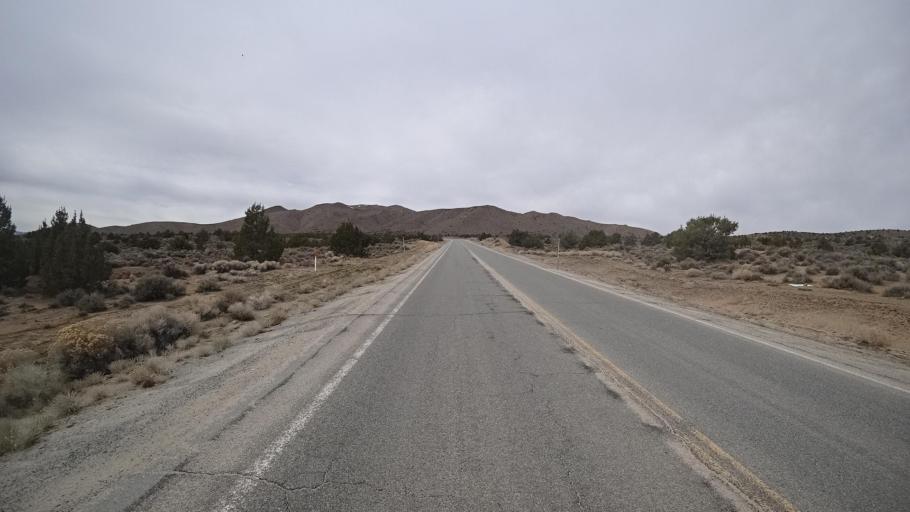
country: US
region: Nevada
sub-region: Washoe County
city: Spanish Springs
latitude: 39.6532
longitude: -119.7356
